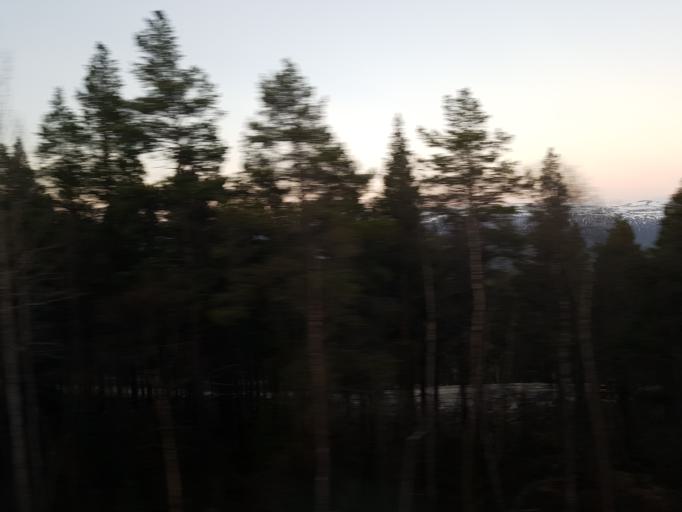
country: NO
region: Oppland
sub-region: Dovre
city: Dombas
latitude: 62.1111
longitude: 9.1034
